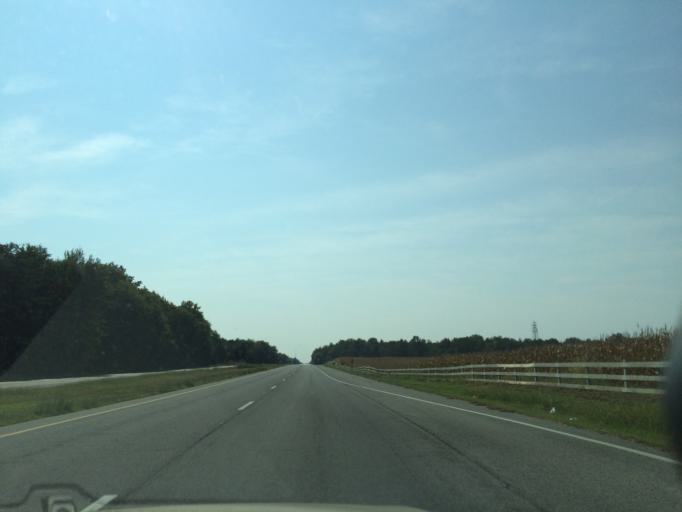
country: US
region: Maryland
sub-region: Charles County
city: La Plata
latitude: 38.4461
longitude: -76.9868
